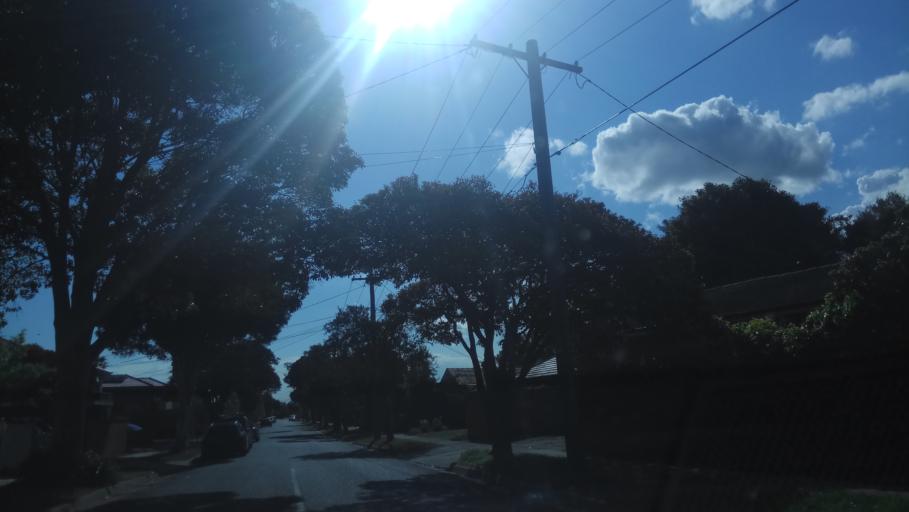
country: AU
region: Victoria
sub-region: Kingston
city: Dingley Village
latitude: -37.9848
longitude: 145.1286
